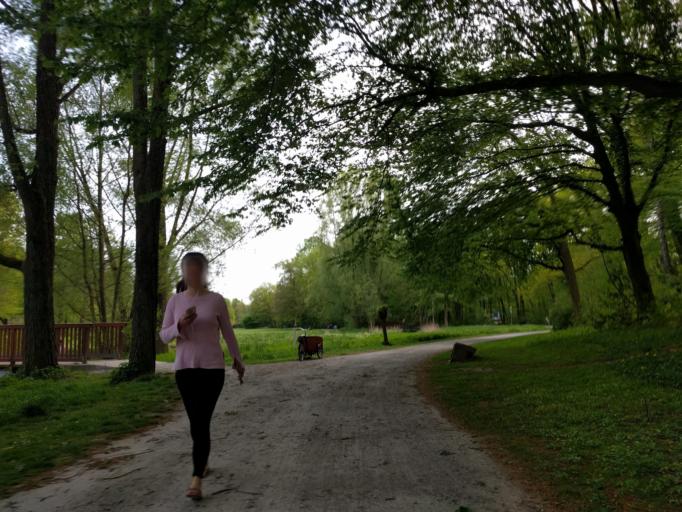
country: DE
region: North Rhine-Westphalia
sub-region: Regierungsbezirk Detmold
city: Bielefeld
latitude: 52.0509
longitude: 8.5326
